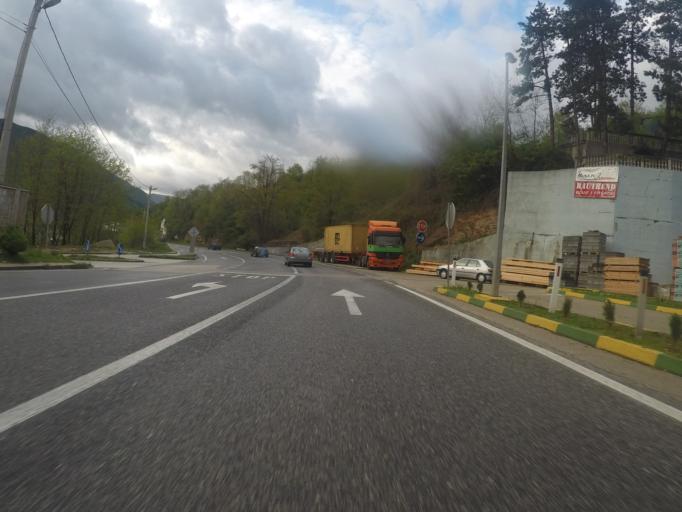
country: BA
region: Federation of Bosnia and Herzegovina
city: Jablanica
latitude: 43.6856
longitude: 17.8315
